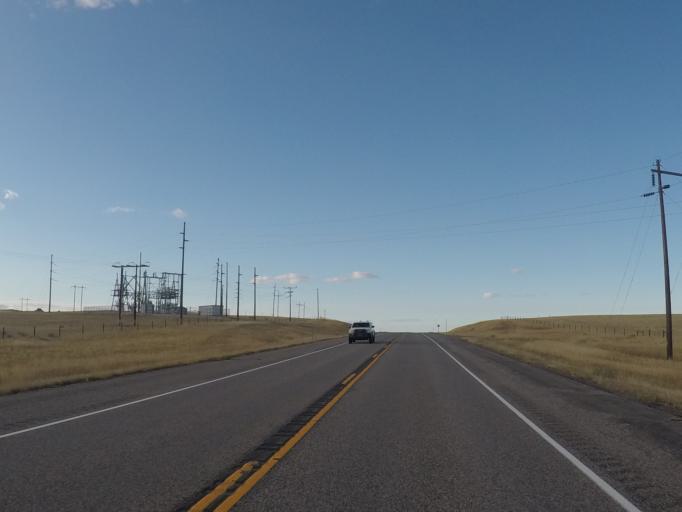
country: US
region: Montana
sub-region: Golden Valley County
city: Ryegate
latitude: 46.2153
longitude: -108.9252
